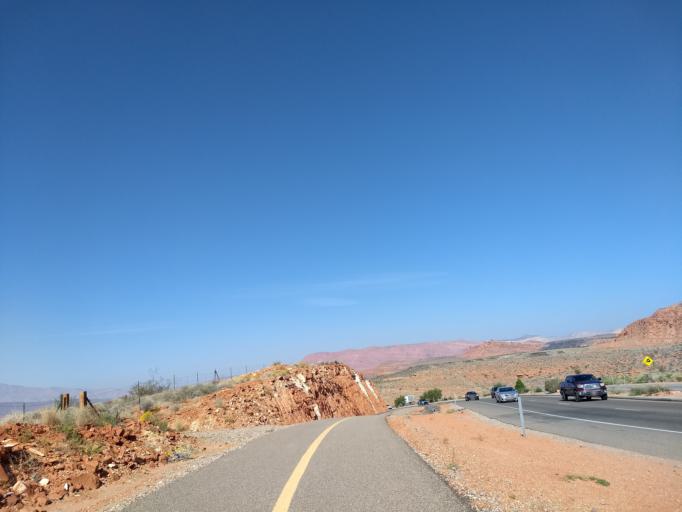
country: US
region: Utah
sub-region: Washington County
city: Saint George
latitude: 37.1347
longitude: -113.5973
